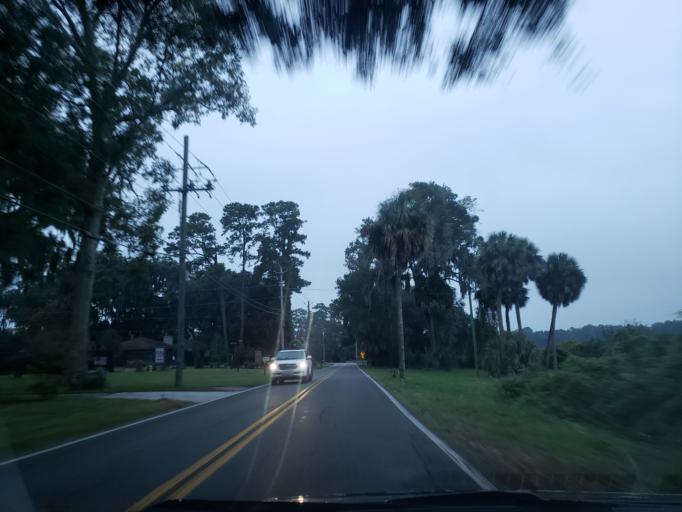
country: US
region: Georgia
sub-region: Chatham County
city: Isle of Hope
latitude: 32.0033
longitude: -81.0636
